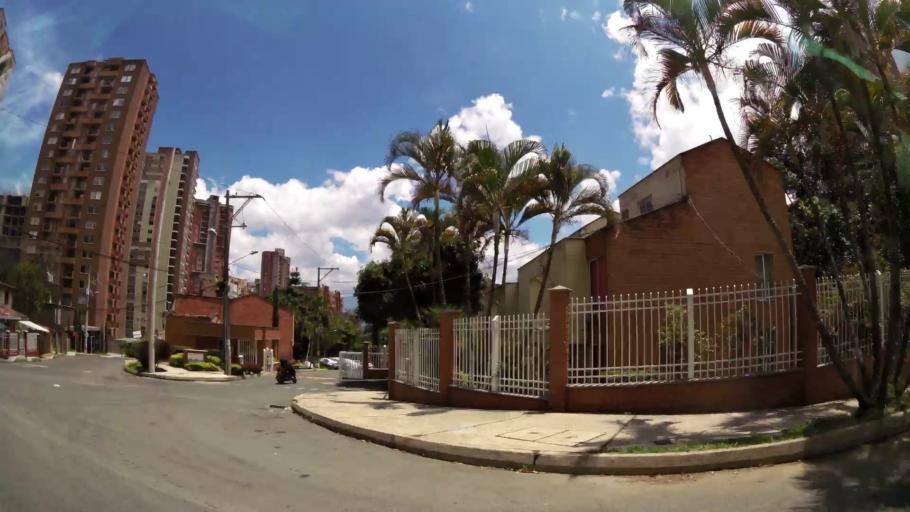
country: CO
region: Antioquia
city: La Estrella
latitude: 6.1641
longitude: -75.6363
